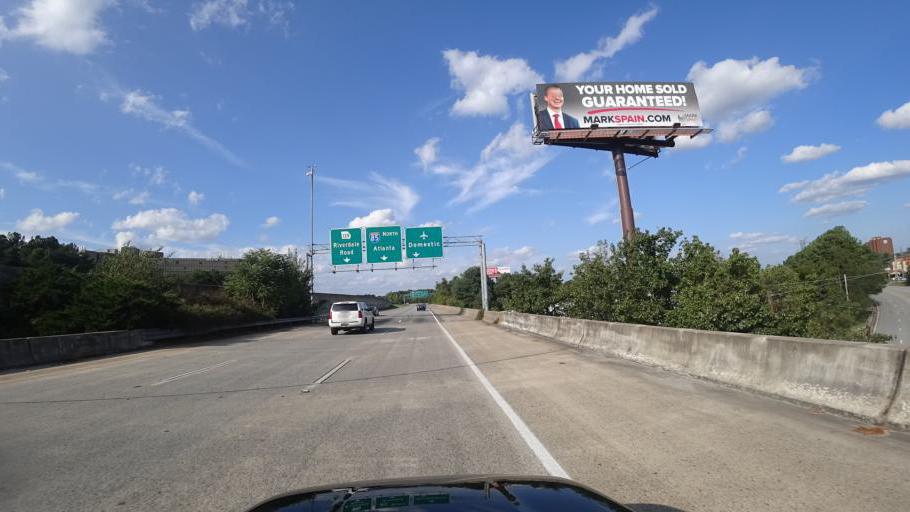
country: US
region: Georgia
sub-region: Fulton County
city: College Park
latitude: 33.6247
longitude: -84.4570
